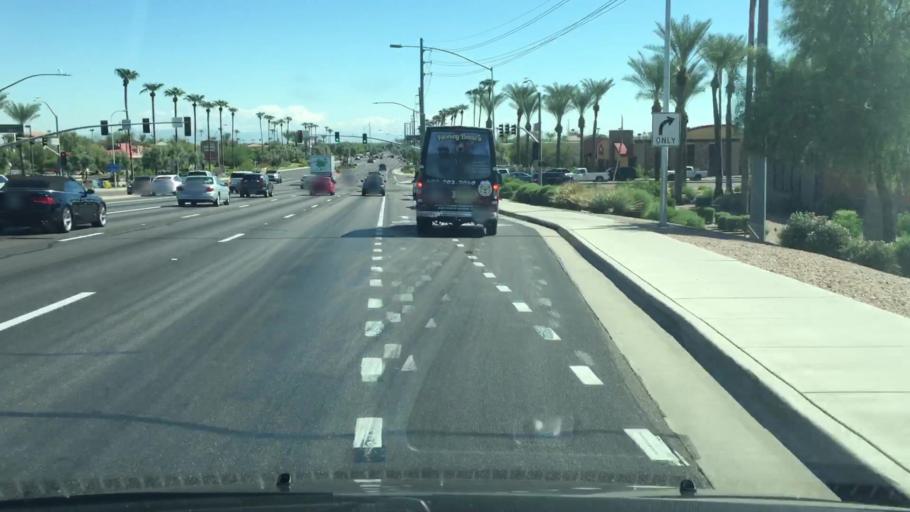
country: US
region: Arizona
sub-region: Maricopa County
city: Guadalupe
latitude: 33.3197
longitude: -111.9696
